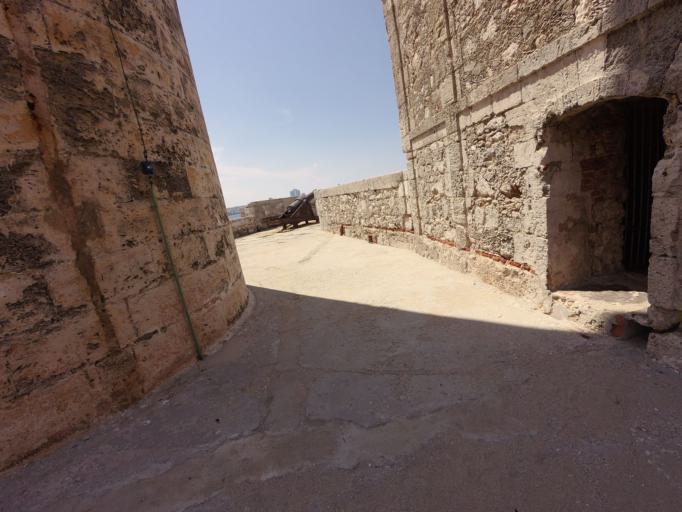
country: CU
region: La Habana
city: Centro Habana
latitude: 23.1503
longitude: -82.3572
